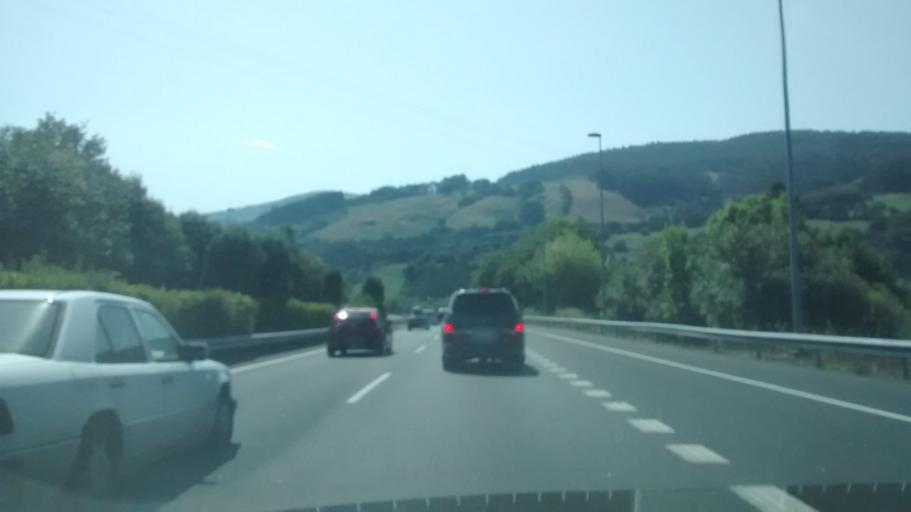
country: ES
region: Cantabria
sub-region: Provincia de Cantabria
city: Laredo
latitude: 43.3958
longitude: -3.3984
